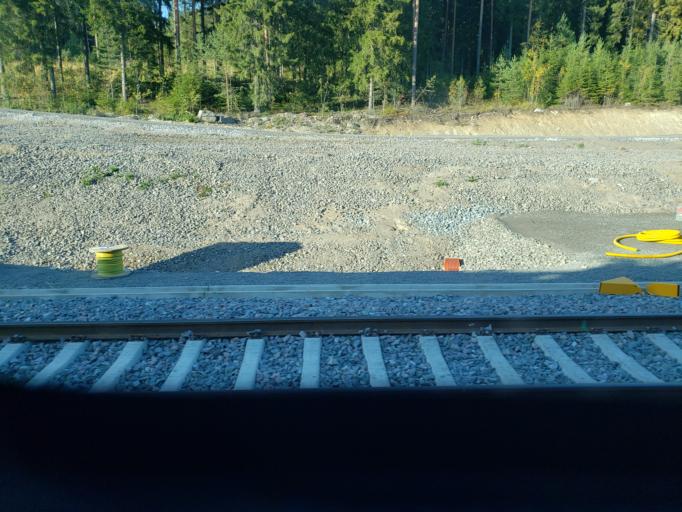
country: FI
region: South Karelia
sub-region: Lappeenranta
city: Lappeenranta
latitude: 60.8582
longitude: 28.3271
